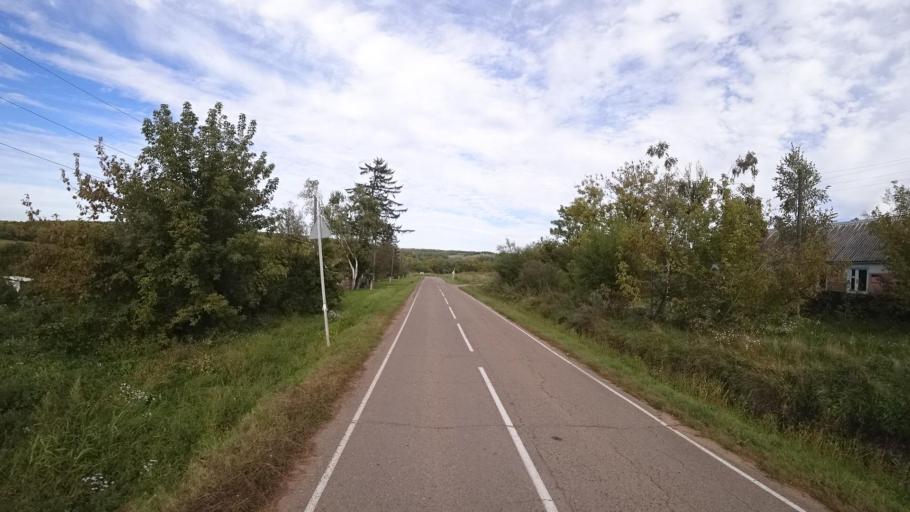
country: RU
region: Primorskiy
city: Dostoyevka
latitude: 44.3288
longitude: 133.4783
